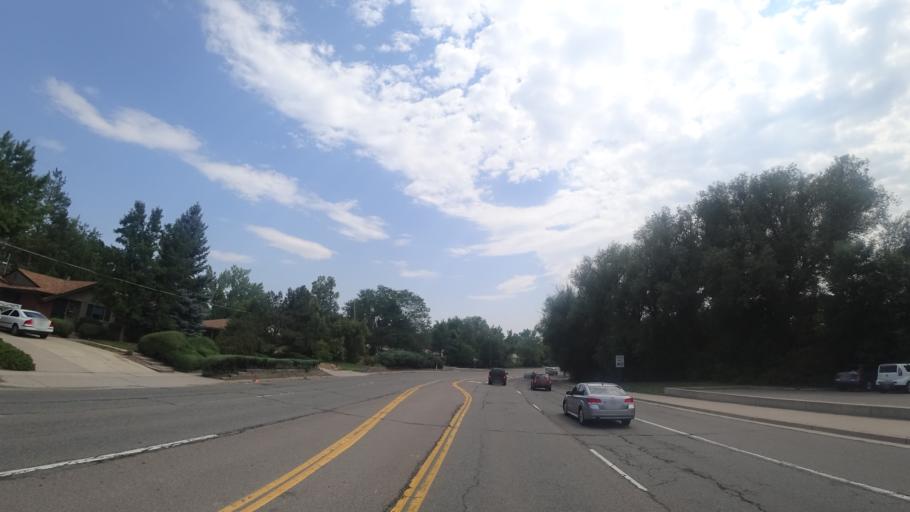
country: US
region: Colorado
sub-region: Arapahoe County
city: Southglenn
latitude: 39.5999
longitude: -104.9575
